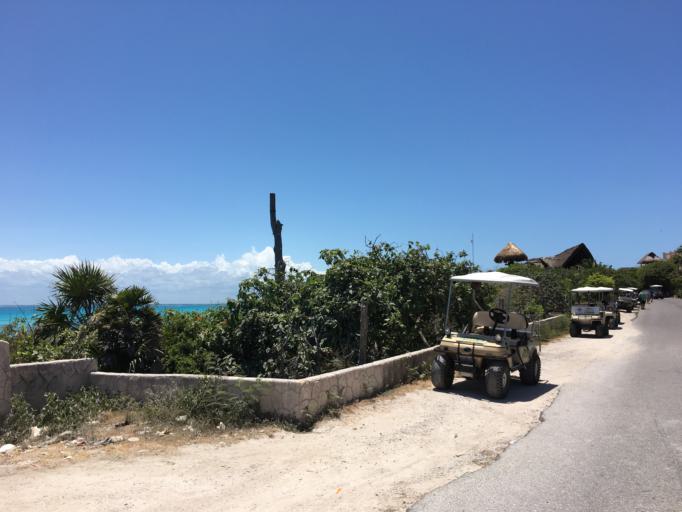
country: MX
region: Quintana Roo
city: Isla Mujeres
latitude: 21.2051
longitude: -86.7158
